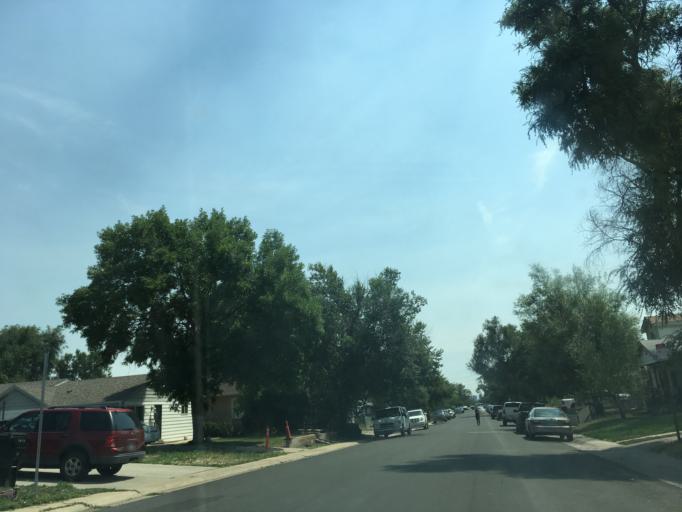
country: US
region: Colorado
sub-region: Jefferson County
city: Lakewood
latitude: 39.7085
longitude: -105.0323
